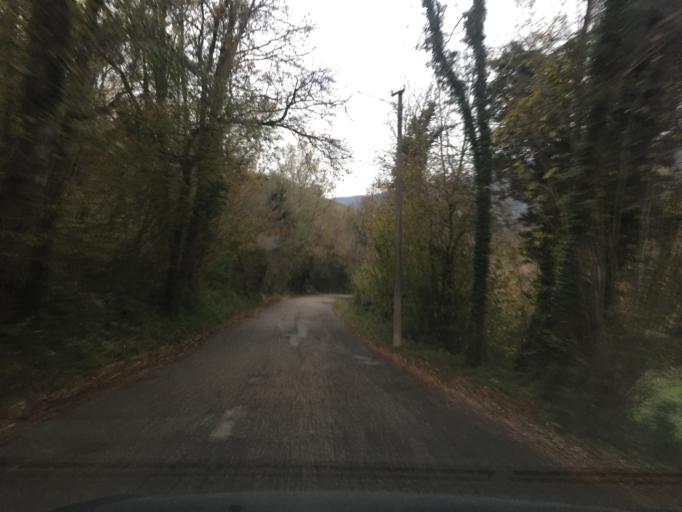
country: IT
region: Friuli Venezia Giulia
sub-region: Provincia di Gorizia
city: Gorizia
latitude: 45.9686
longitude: 13.6198
